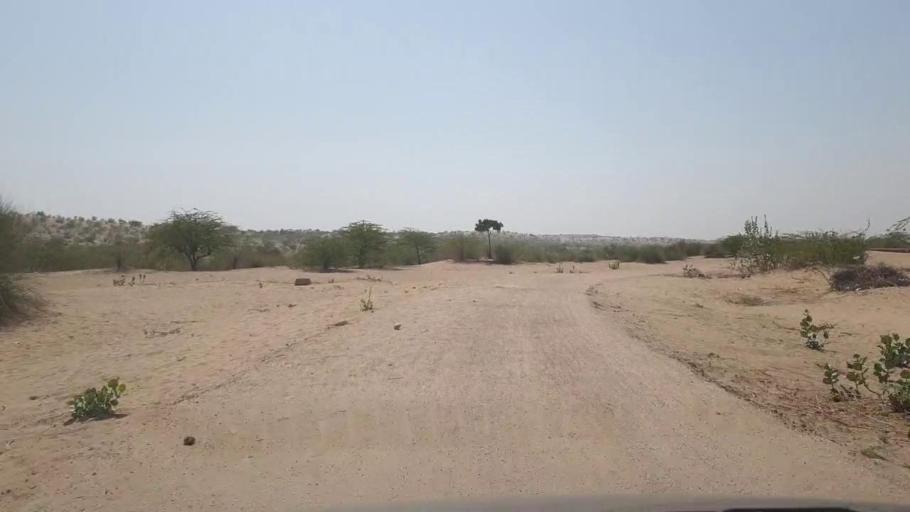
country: PK
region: Sindh
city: Chor
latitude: 25.5623
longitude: 70.1786
